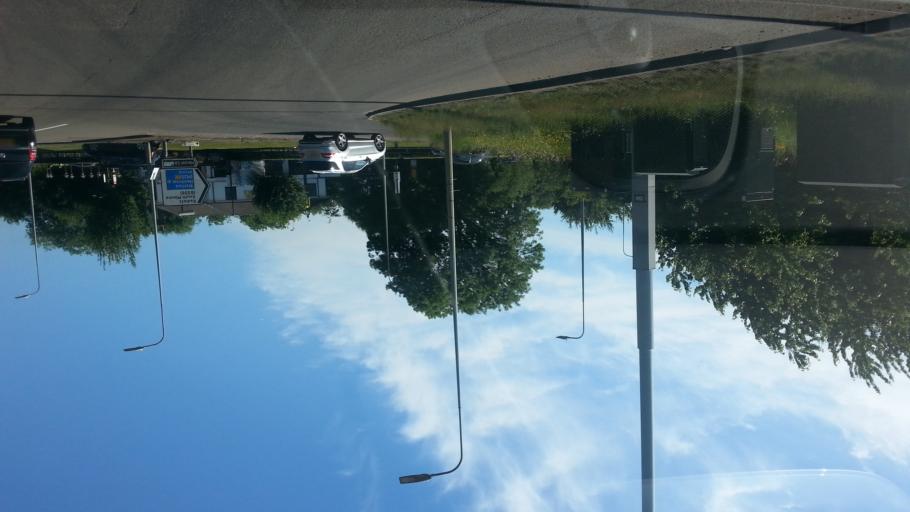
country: GB
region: England
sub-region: Hertfordshire
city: Shenley AV
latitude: 51.7176
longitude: -0.2783
